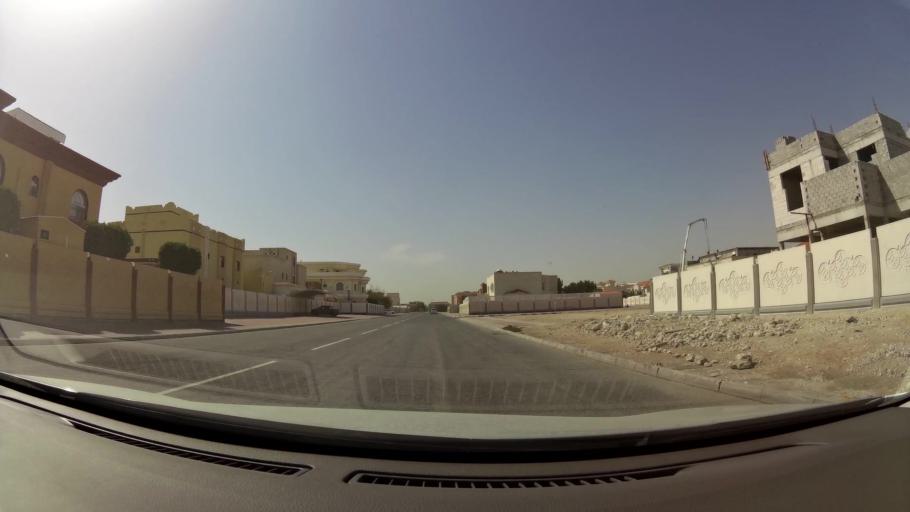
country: QA
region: Baladiyat ad Dawhah
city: Doha
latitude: 25.3557
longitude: 51.5039
